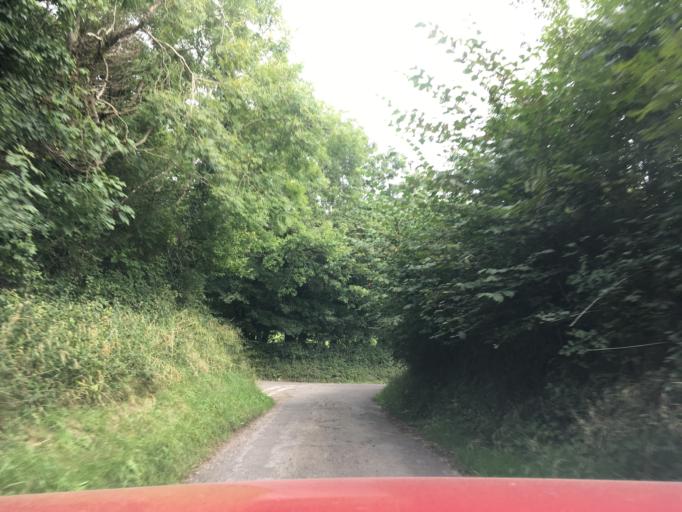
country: GB
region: England
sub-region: South Gloucestershire
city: Falfield
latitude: 51.6114
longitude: -2.4556
